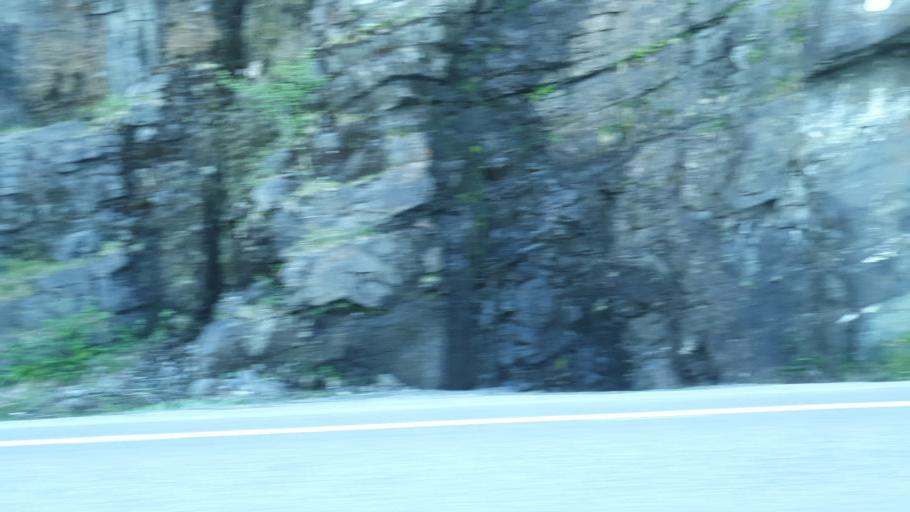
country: NO
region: Sor-Trondelag
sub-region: Rissa
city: Rissa
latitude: 63.5057
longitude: 10.1308
